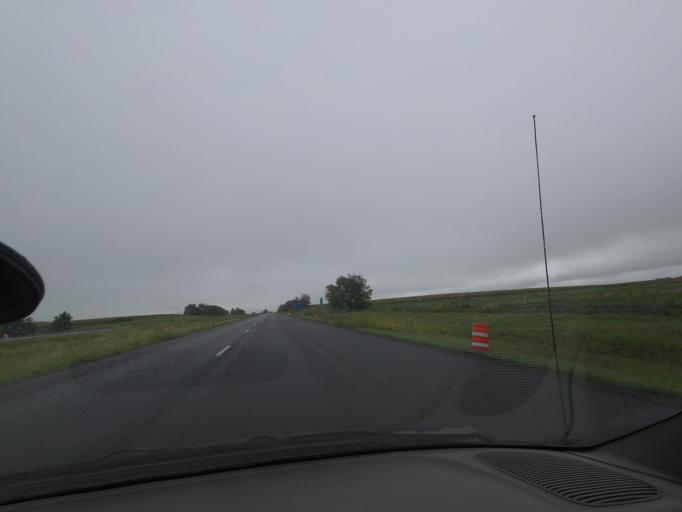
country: US
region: Illinois
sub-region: Macon County
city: Harristown
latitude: 39.8312
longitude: -89.0933
